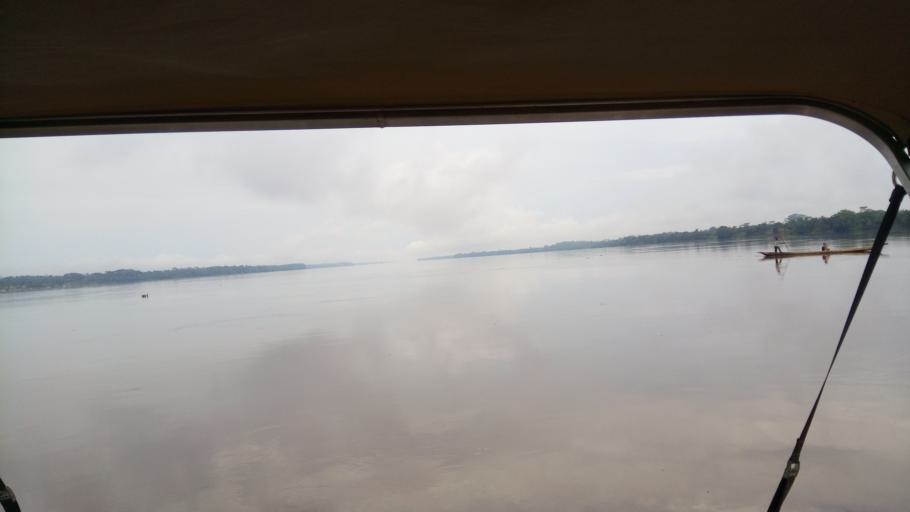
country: CD
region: Eastern Province
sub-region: Sous-Region de la Tshopo
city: Yangambi
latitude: 0.6021
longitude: 24.7290
